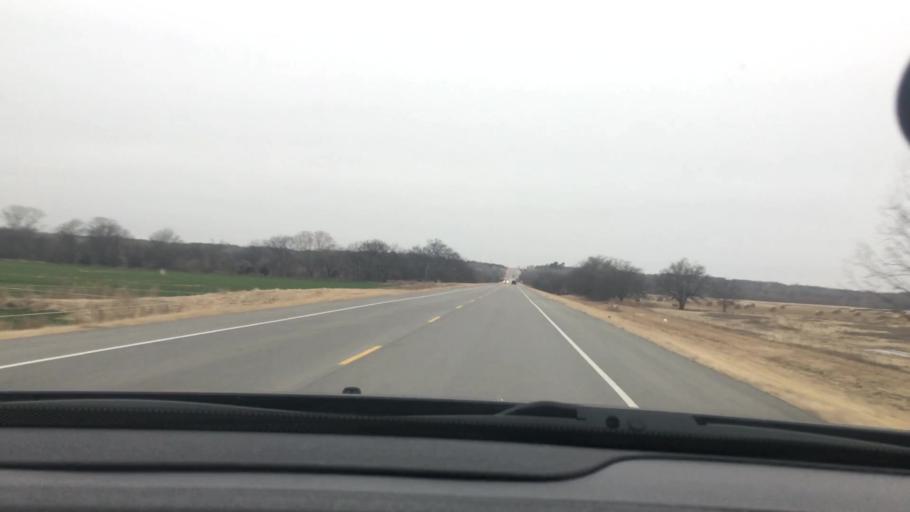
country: US
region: Oklahoma
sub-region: Garvin County
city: Wynnewood
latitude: 34.6227
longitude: -97.1883
